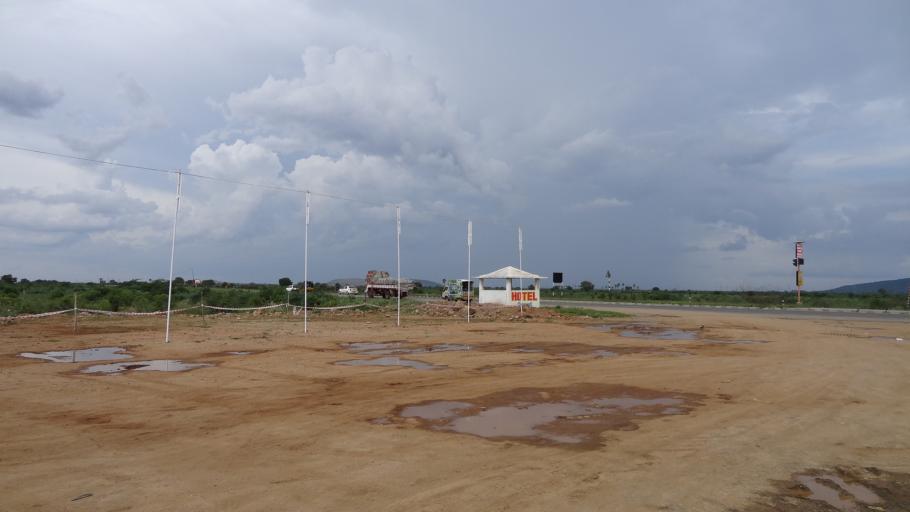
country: IN
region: Tamil Nadu
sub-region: Thoothukkudi
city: Kovilpatti
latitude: 9.1135
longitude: 77.8118
